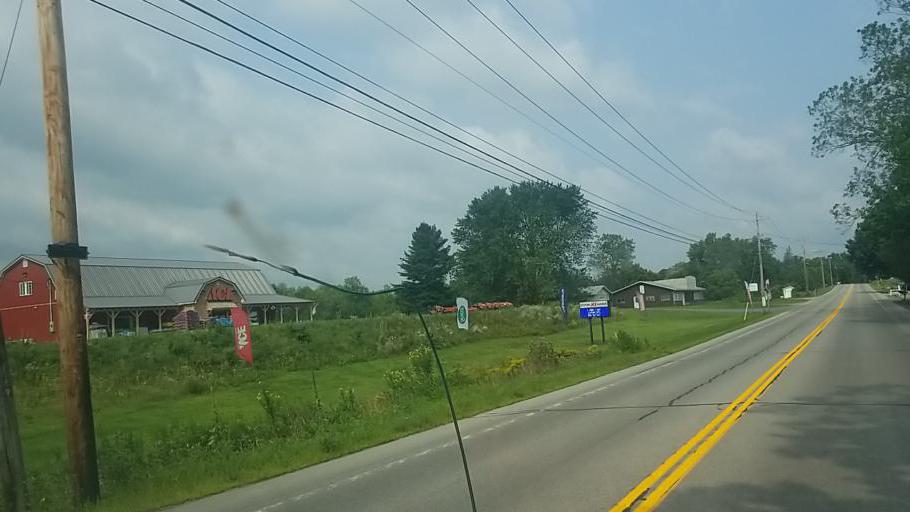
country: US
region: New York
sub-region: Montgomery County
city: Fort Plain
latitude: 42.9205
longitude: -74.5976
